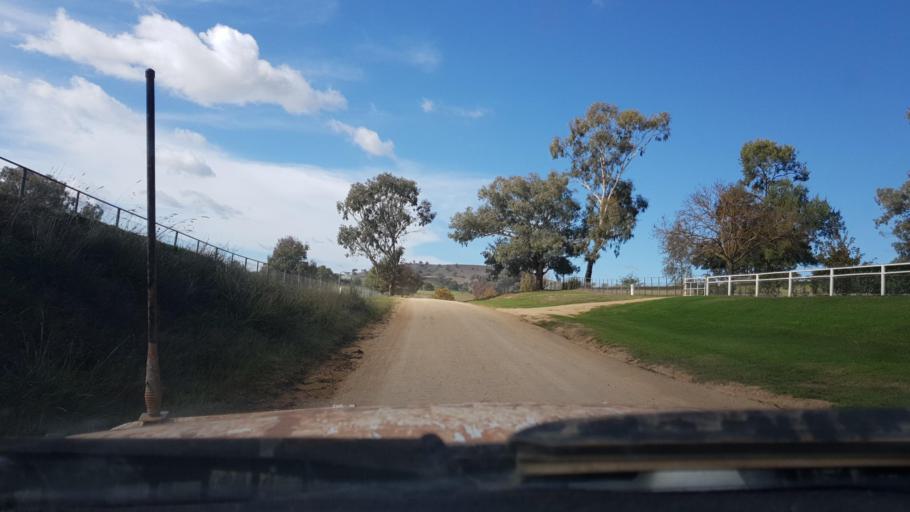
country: AU
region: New South Wales
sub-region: Boorowa
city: Boorowa
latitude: -34.1483
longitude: 148.8105
